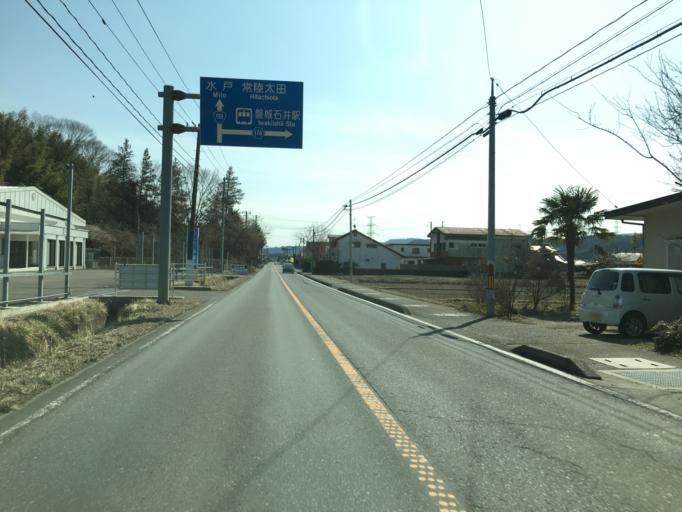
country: JP
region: Ibaraki
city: Daigo
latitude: 36.9064
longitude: 140.4179
